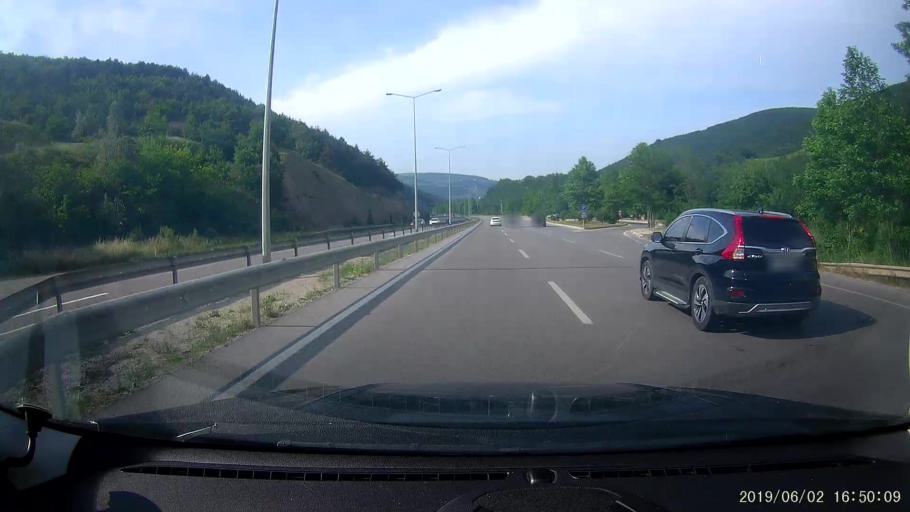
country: TR
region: Samsun
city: Samsun
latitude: 41.2486
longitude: 36.1732
